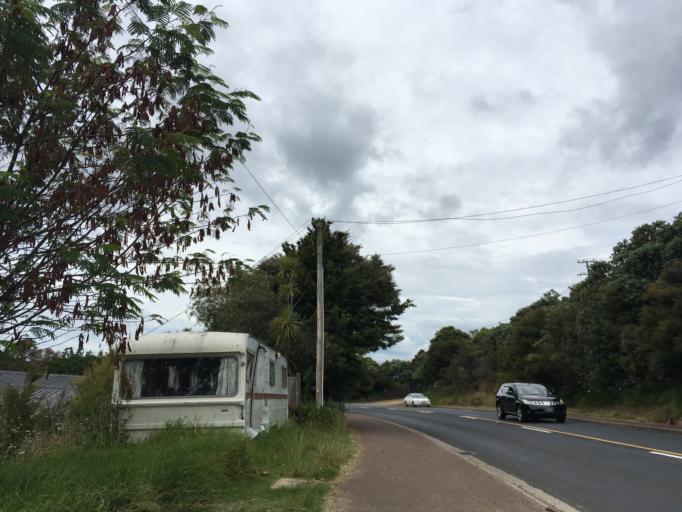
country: NZ
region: Auckland
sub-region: Auckland
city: Pakuranga
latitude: -36.7979
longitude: 175.0329
